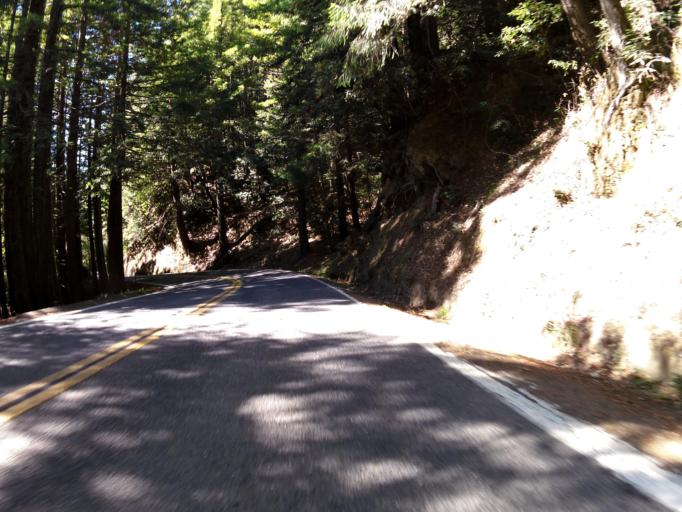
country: US
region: California
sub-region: Humboldt County
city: Redway
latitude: 39.7956
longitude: -123.8124
